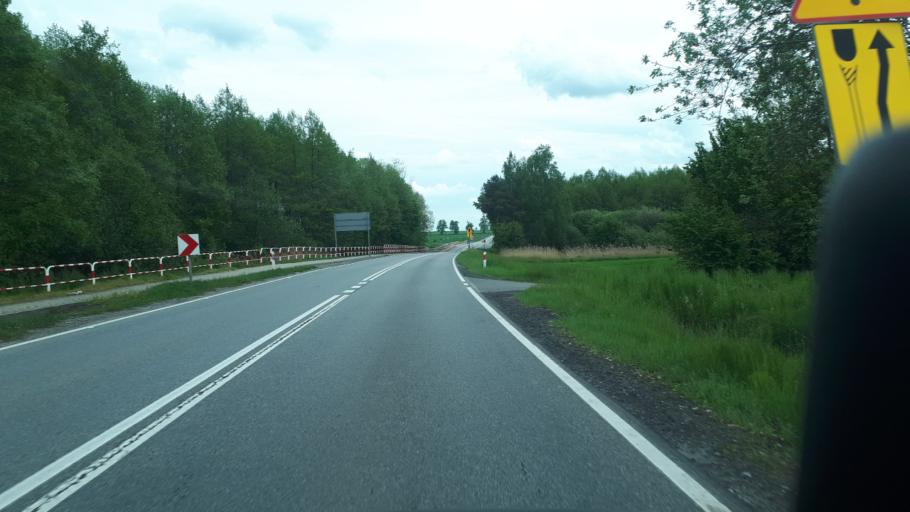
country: PL
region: Greater Poland Voivodeship
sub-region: Powiat kepinski
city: Opatow
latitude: 51.2073
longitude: 18.1471
